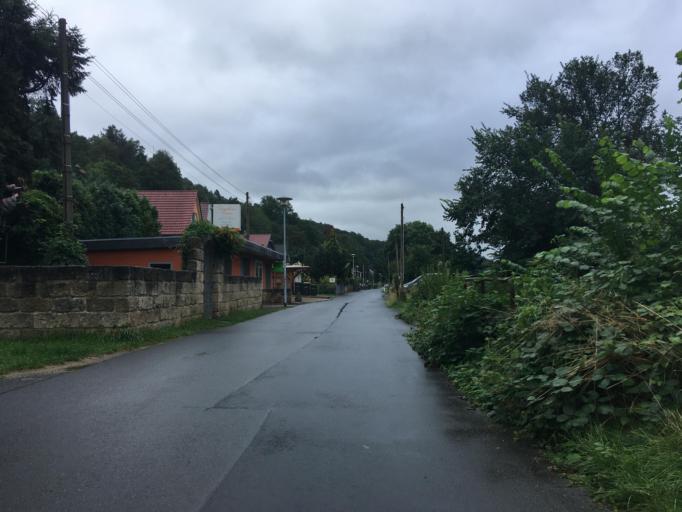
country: DE
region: Saxony
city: Pirna
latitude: 50.9637
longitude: 13.9636
